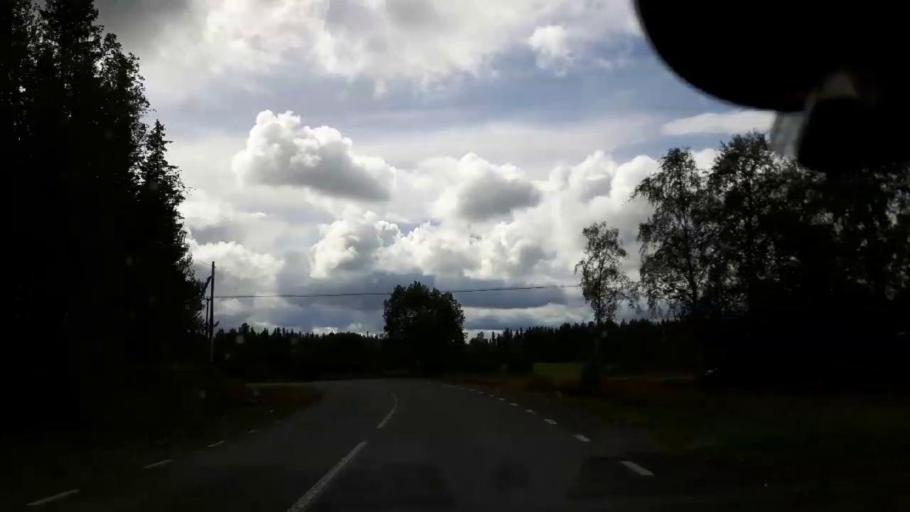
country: SE
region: Jaemtland
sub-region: Krokoms Kommun
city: Valla
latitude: 63.4317
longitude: 13.8073
